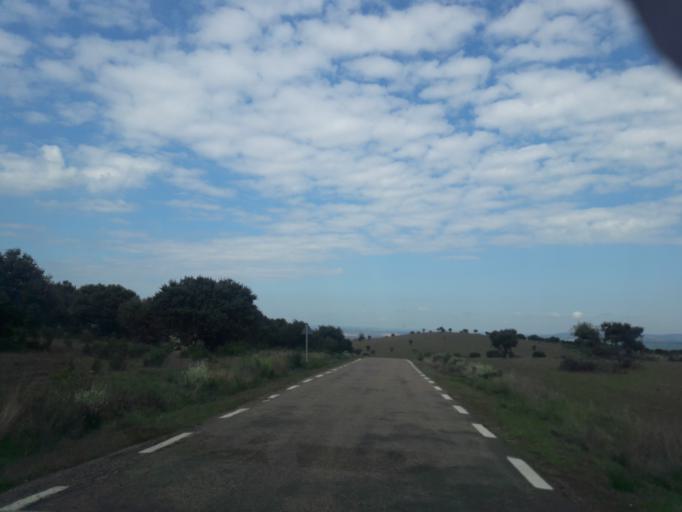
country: ES
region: Castille and Leon
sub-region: Provincia de Salamanca
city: Serradilla del Arroyo
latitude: 40.5426
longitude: -6.4062
